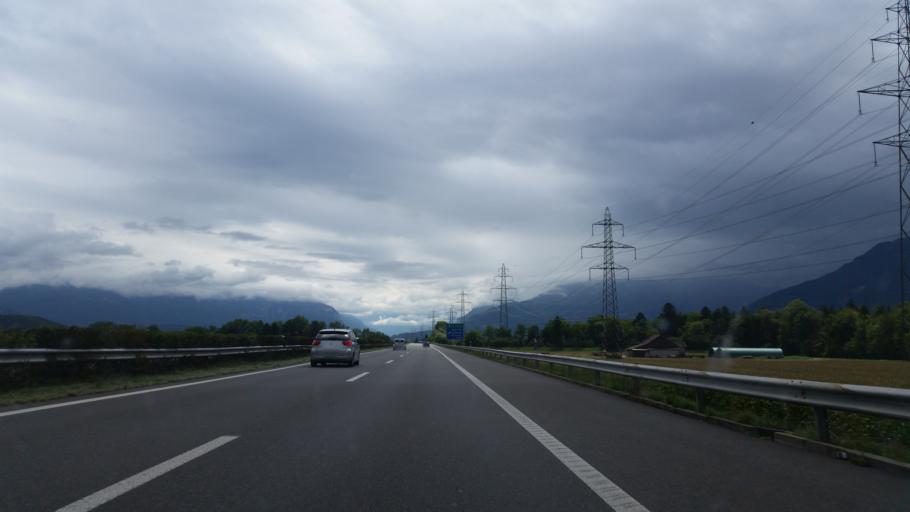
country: CH
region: Vaud
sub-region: Aigle District
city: Aigle
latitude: 46.3287
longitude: 6.9357
